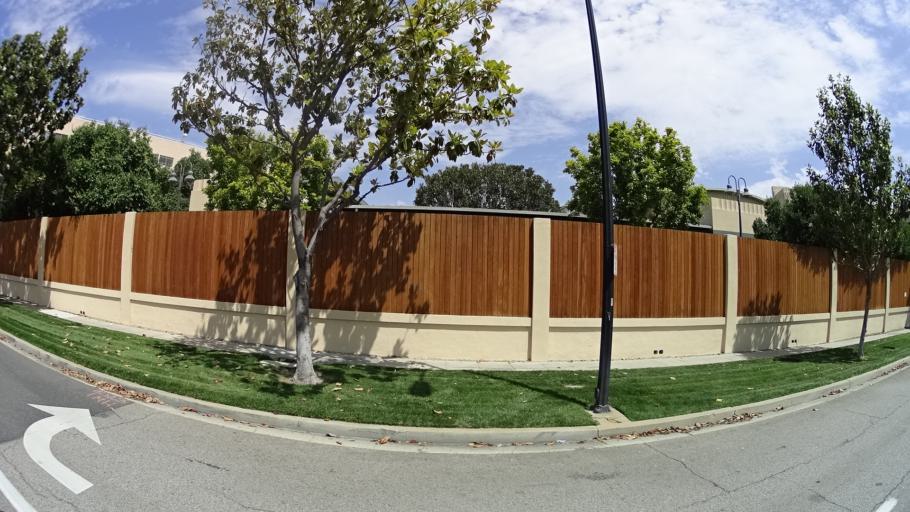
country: US
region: California
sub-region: Los Angeles County
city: Burbank
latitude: 34.1559
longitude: -118.3236
